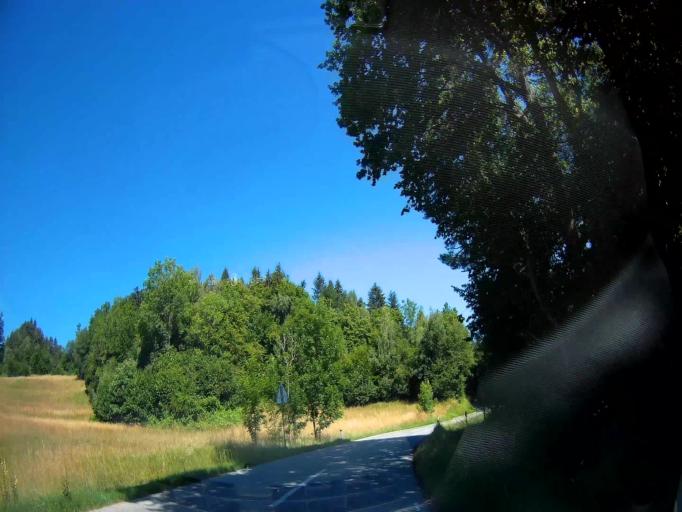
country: AT
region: Carinthia
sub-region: Politischer Bezirk Klagenfurt Land
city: Maria Worth
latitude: 46.5993
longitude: 14.1516
